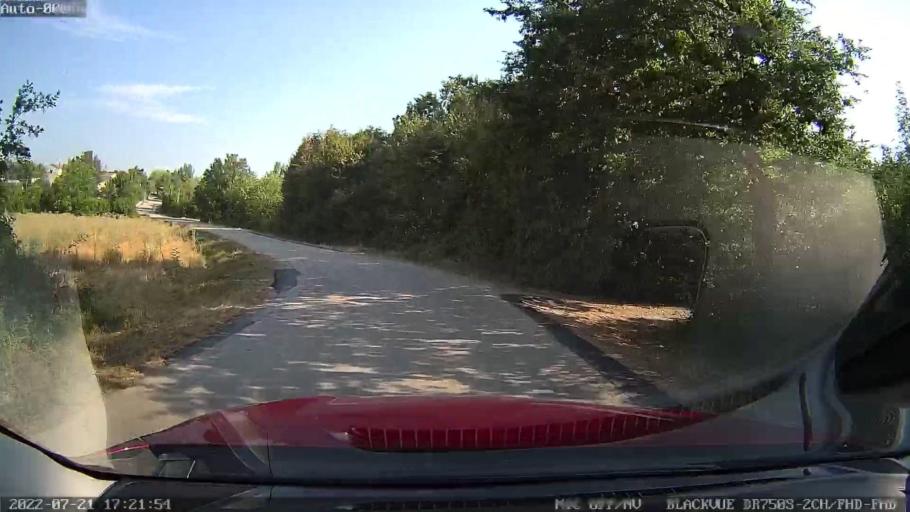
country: HR
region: Istarska
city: Karojba
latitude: 45.1913
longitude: 13.8278
